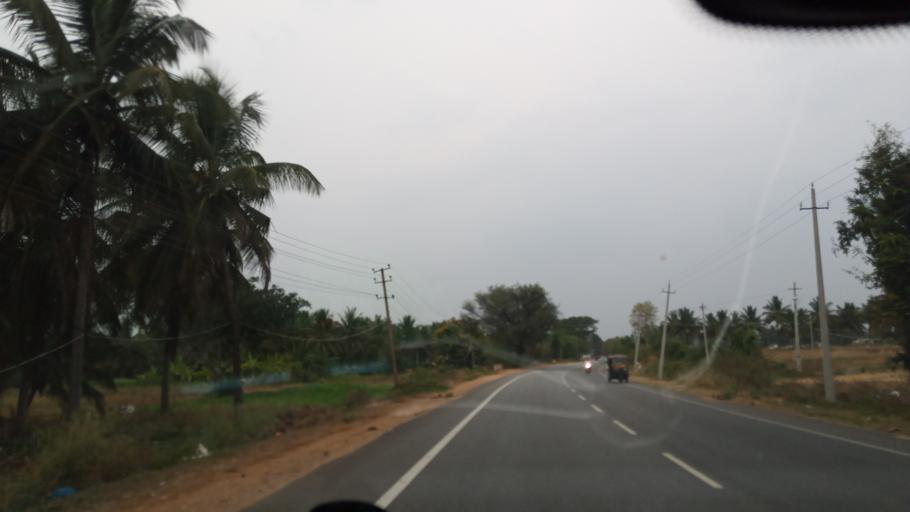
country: IN
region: Karnataka
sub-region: Mandya
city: Nagamangala
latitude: 12.8012
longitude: 76.7517
